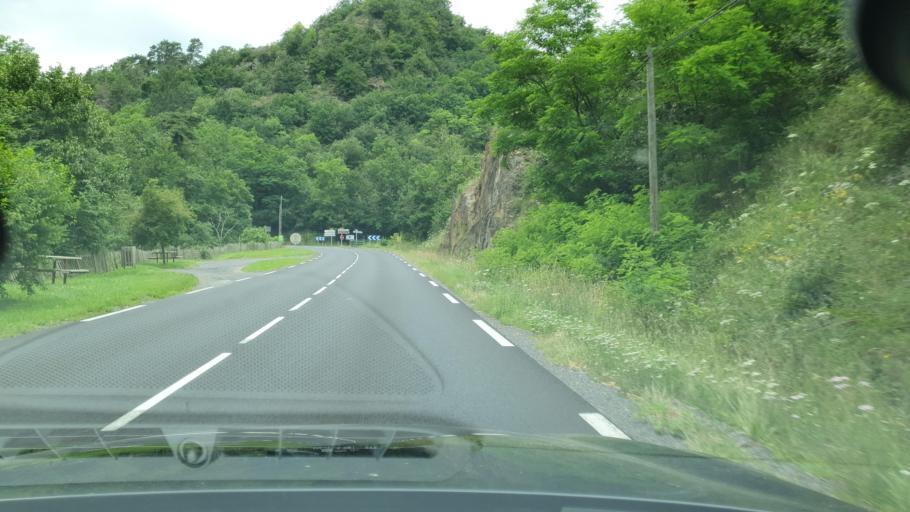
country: FR
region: Auvergne
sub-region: Departement du Puy-de-Dome
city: Champeix
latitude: 45.5793
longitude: 3.0745
